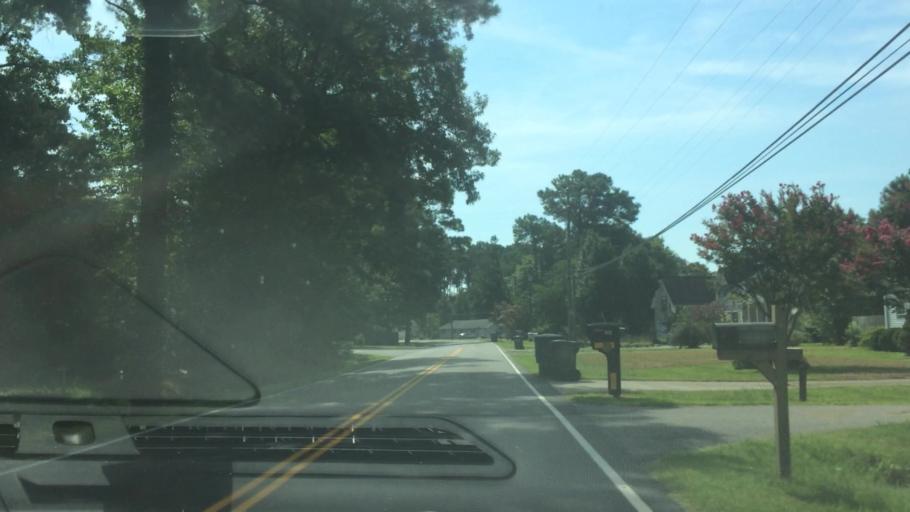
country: US
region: Virginia
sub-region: City of Poquoson
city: Poquoson
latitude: 37.1633
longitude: -76.4272
